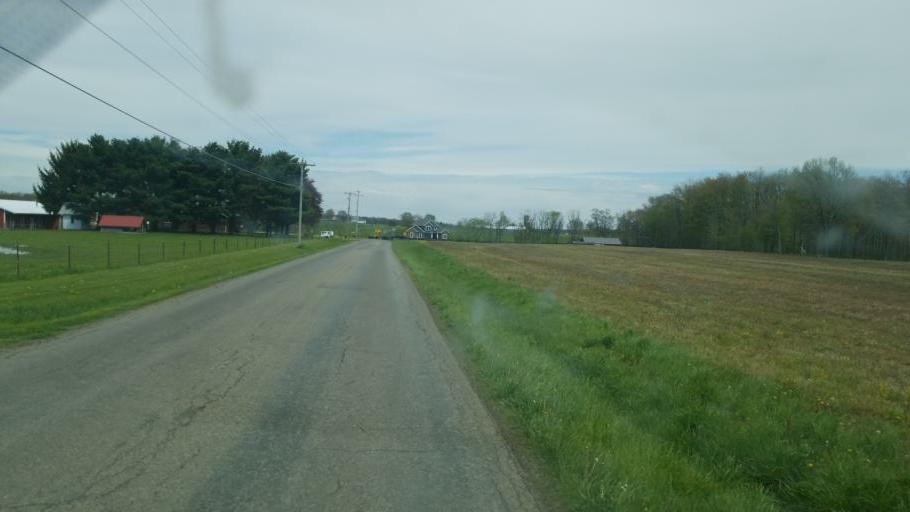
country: US
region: Ohio
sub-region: Wayne County
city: Apple Creek
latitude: 40.7300
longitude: -81.9103
